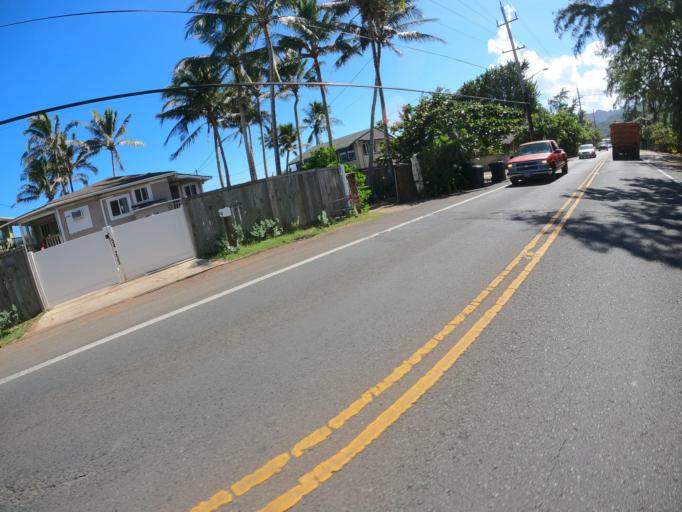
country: US
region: Hawaii
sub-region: Honolulu County
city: Hau'ula
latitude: 21.6161
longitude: -157.9135
